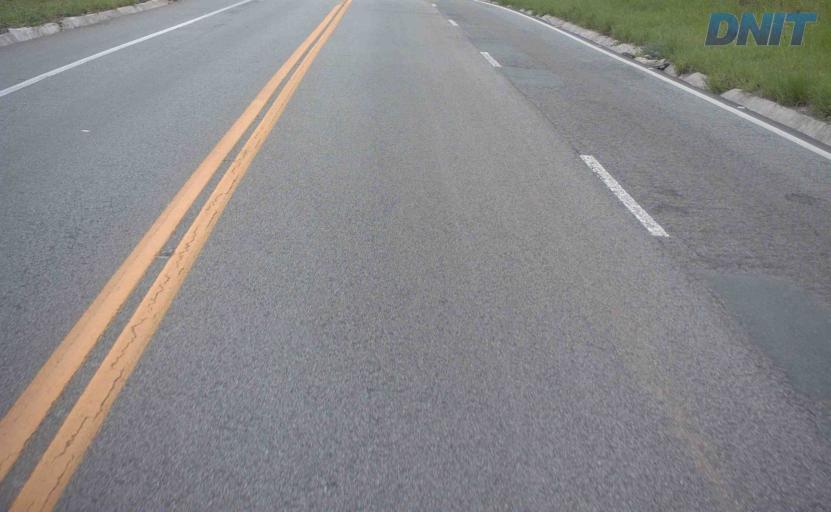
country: BR
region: Minas Gerais
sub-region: Nova Era
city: Nova Era
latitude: -19.6317
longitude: -42.8966
